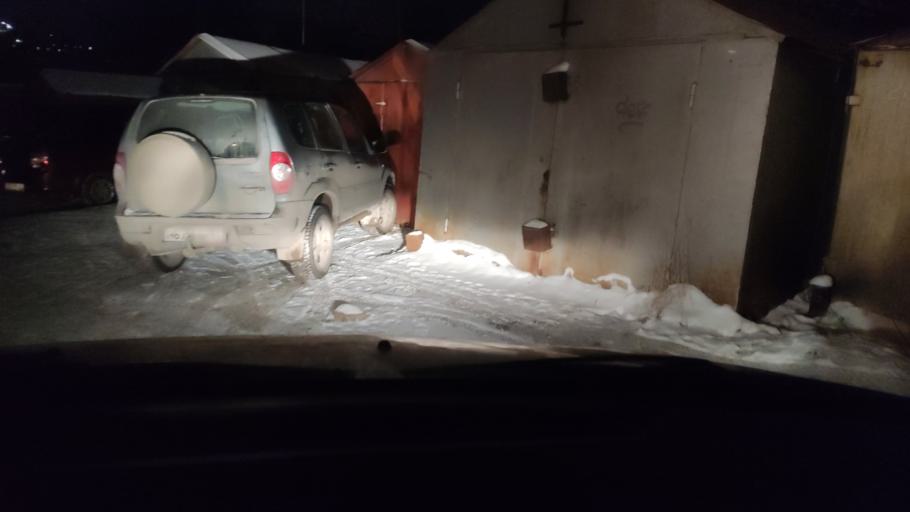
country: RU
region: Perm
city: Perm
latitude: 57.9740
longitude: 56.2249
